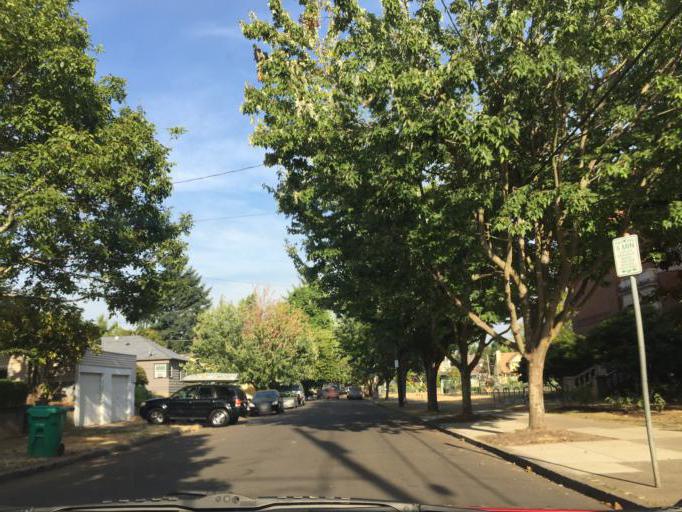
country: US
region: Oregon
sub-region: Multnomah County
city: Portland
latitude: 45.5250
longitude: -122.6403
